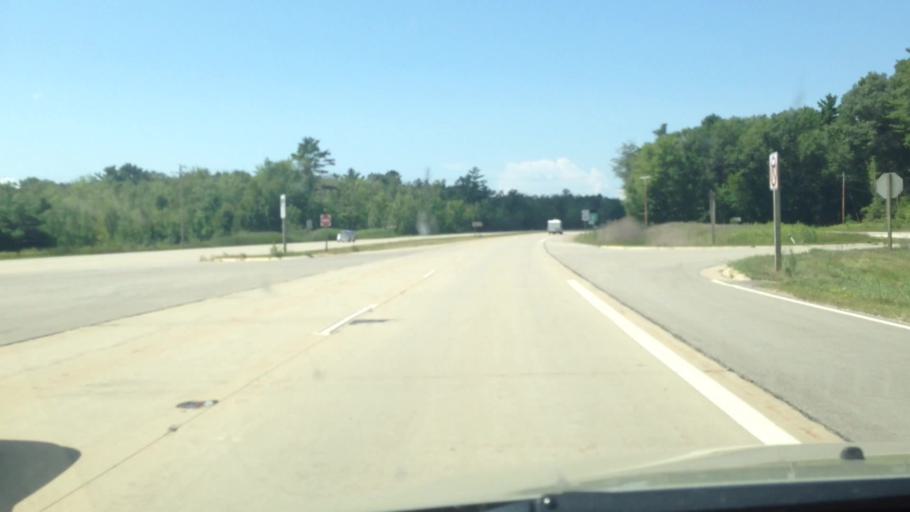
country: US
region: Wisconsin
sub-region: Oconto County
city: Oconto
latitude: 44.8170
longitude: -87.9445
